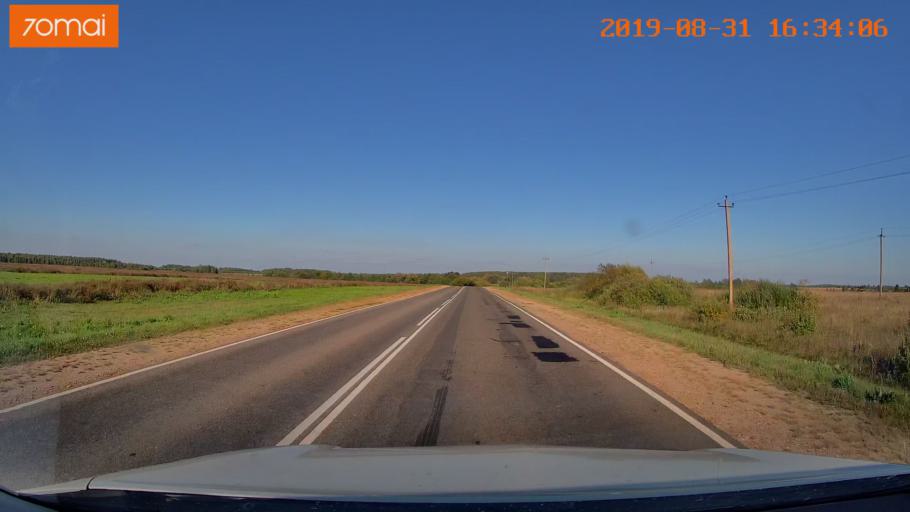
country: RU
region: Kaluga
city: Kurovskoye
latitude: 54.5264
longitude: 35.9090
